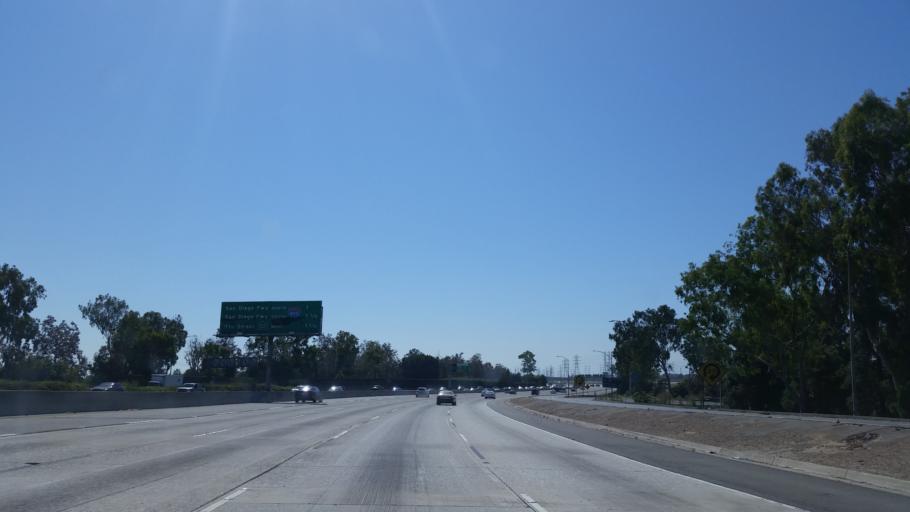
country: US
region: California
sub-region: Orange County
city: Los Alamitos
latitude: 33.8029
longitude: -118.0820
